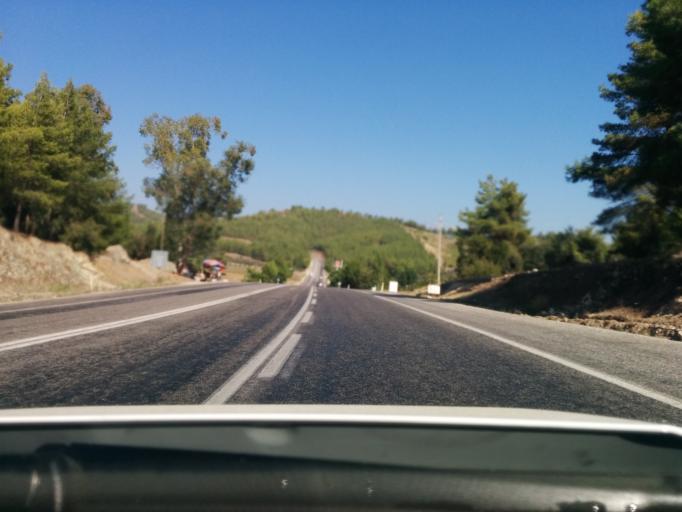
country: TR
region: Mugla
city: Kemer
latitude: 36.6099
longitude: 29.3586
